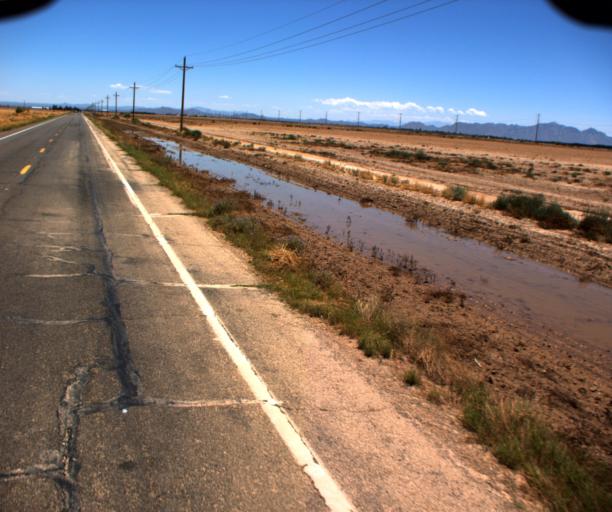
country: US
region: Arizona
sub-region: Pinal County
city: Coolidge
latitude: 32.8797
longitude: -111.6092
